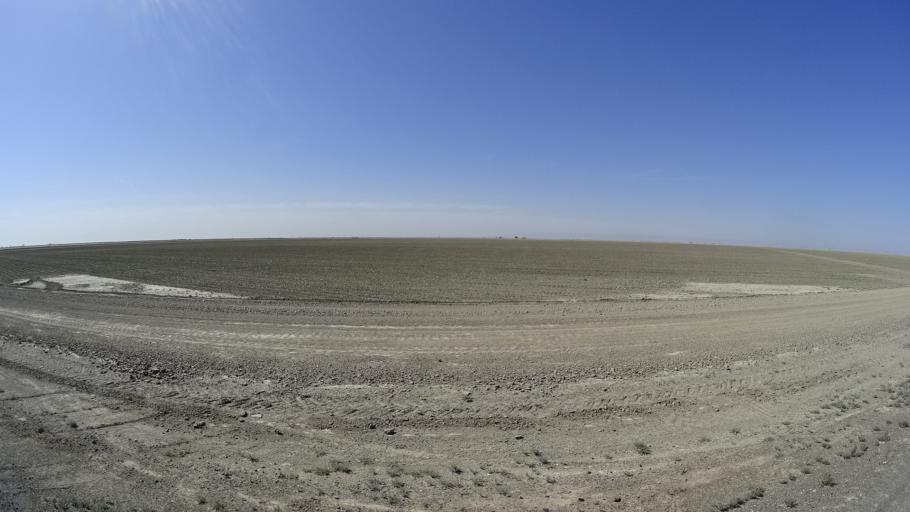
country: US
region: California
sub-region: Tulare County
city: Alpaugh
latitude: 35.8914
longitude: -119.5498
